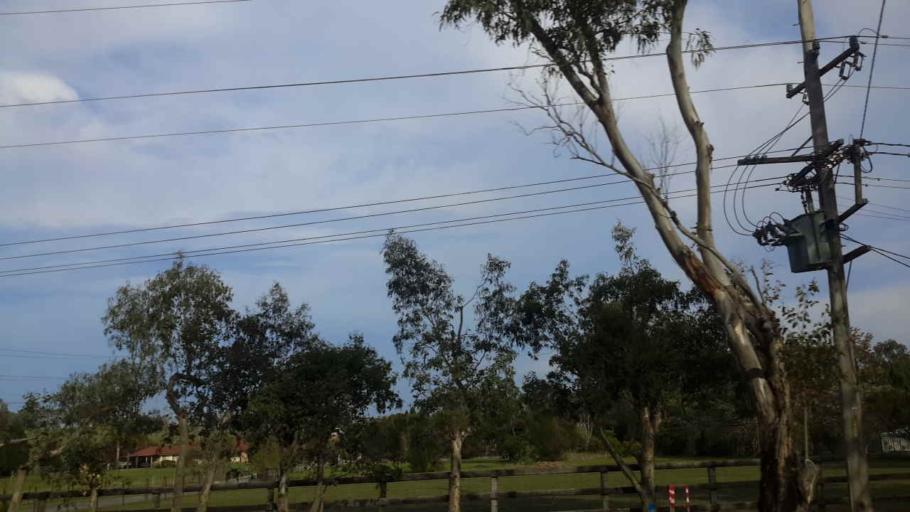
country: AU
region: New South Wales
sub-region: Penrith Municipality
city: Glenmore Park
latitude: -33.7959
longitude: 150.6985
